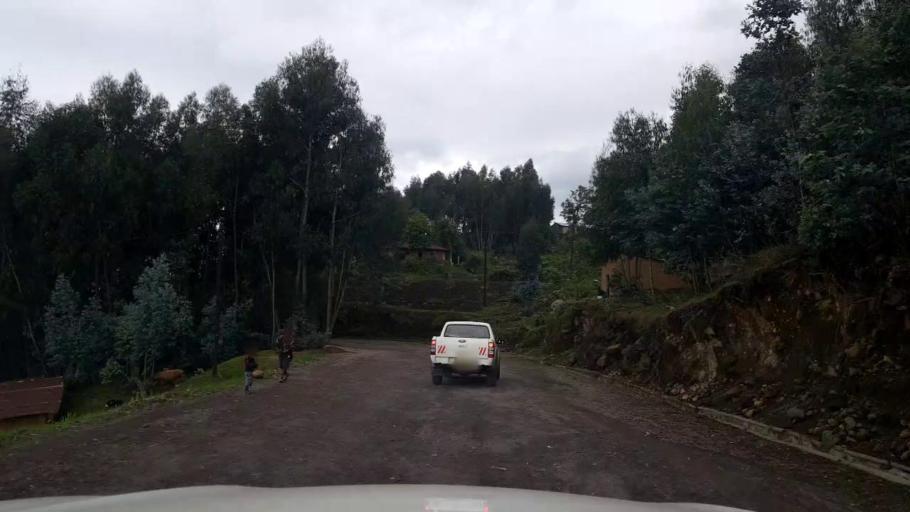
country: RW
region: Northern Province
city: Musanze
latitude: -1.4943
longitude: 29.5325
